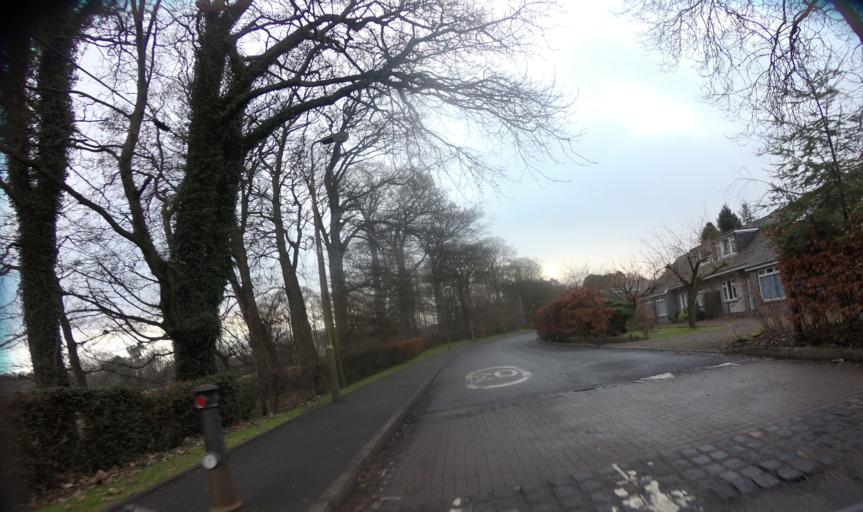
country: GB
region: Scotland
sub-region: West Lothian
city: Livingston
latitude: 55.8677
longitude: -3.5257
